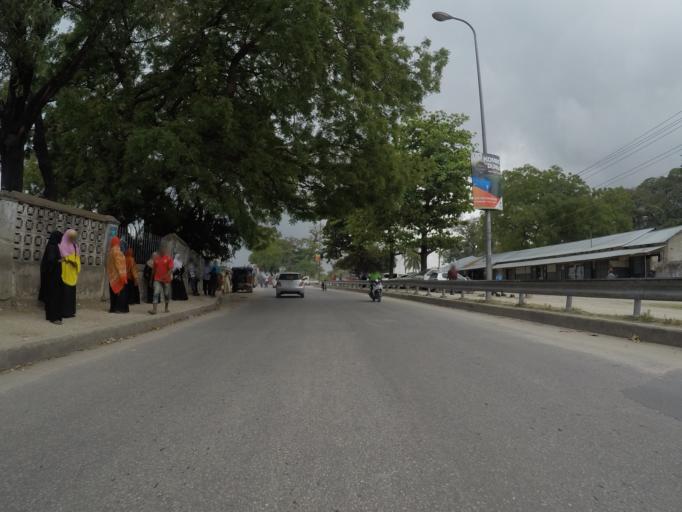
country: TZ
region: Zanzibar Urban/West
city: Zanzibar
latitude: -6.1533
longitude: 39.2087
